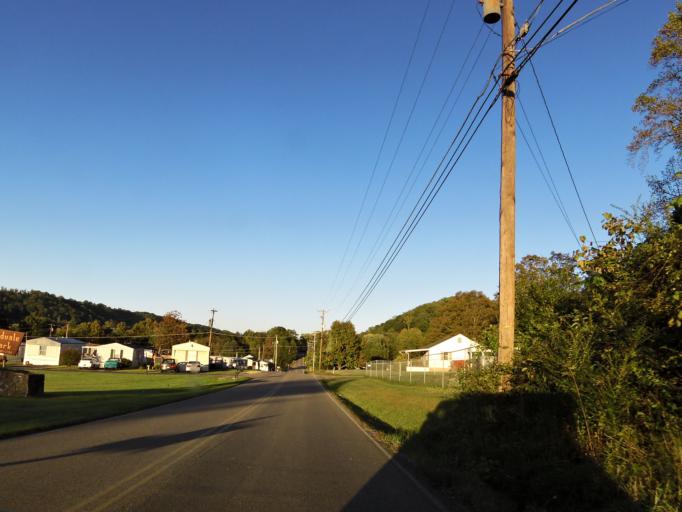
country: US
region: Tennessee
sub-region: Knox County
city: Knoxville
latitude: 36.0557
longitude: -83.9298
